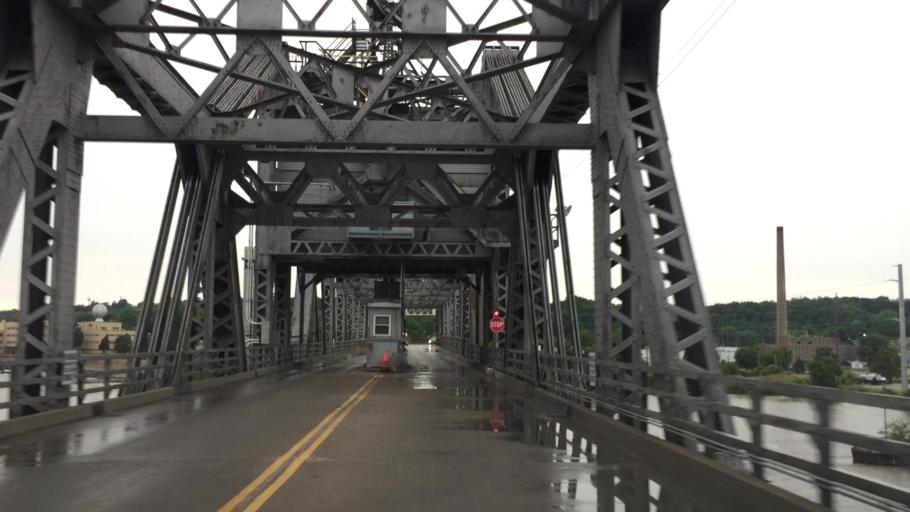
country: US
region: Iowa
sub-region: Lee County
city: Fort Madison
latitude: 40.6280
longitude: -91.2970
